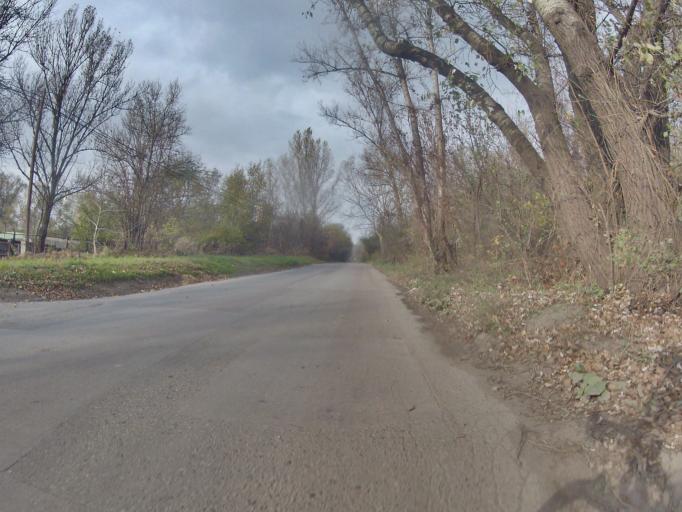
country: PL
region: Lesser Poland Voivodeship
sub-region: Powiat wielicki
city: Wegrzce Wielkie
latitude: 50.0669
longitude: 20.1023
